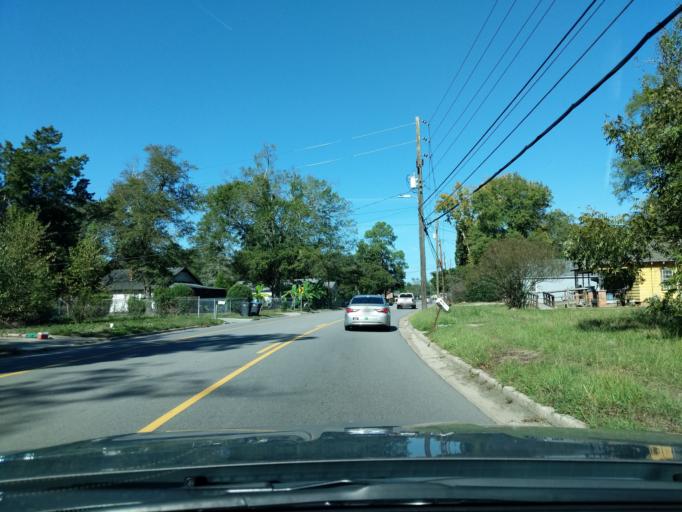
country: US
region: Georgia
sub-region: Richmond County
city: Augusta
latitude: 33.4436
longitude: -82.0046
